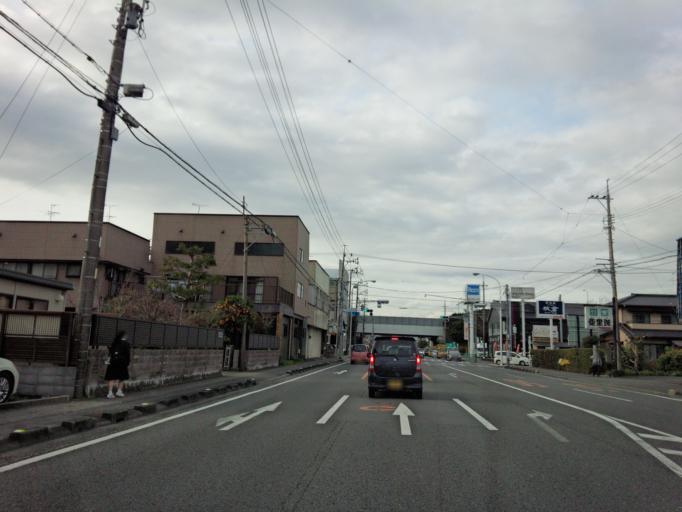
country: JP
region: Shizuoka
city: Shizuoka-shi
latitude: 34.9448
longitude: 138.3925
